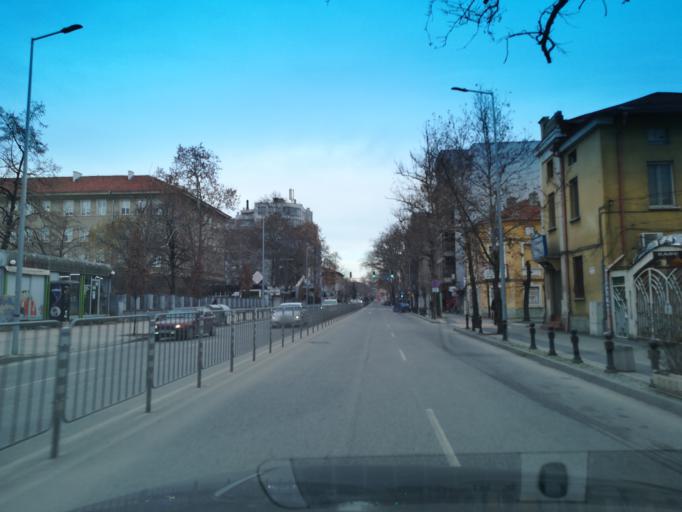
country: BG
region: Plovdiv
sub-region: Obshtina Plovdiv
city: Plovdiv
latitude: 42.1369
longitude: 24.7411
